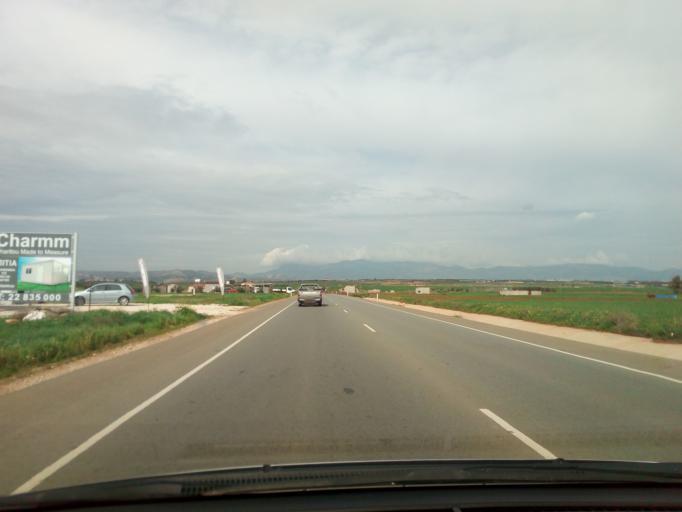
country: CY
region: Lefkosia
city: Akaki
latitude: 35.1478
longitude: 33.1557
